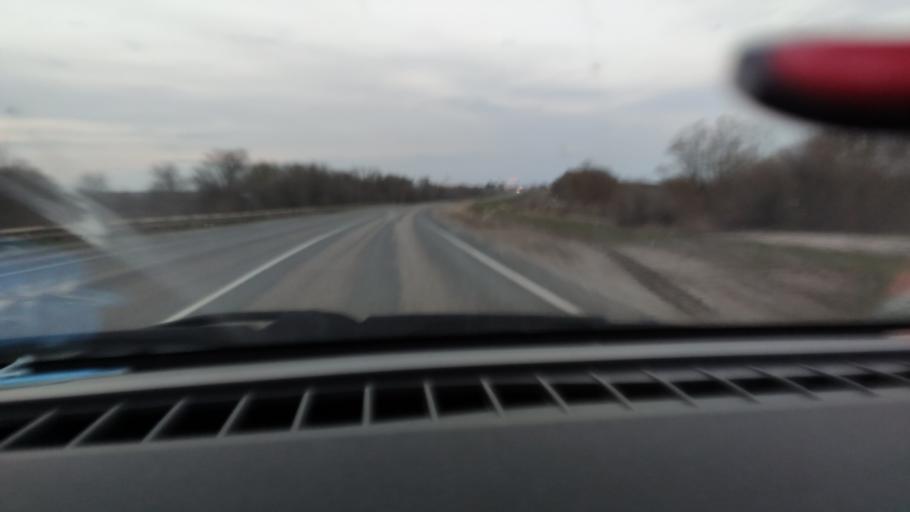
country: RU
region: Saratov
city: Sinodskoye
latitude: 51.9799
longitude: 46.6546
